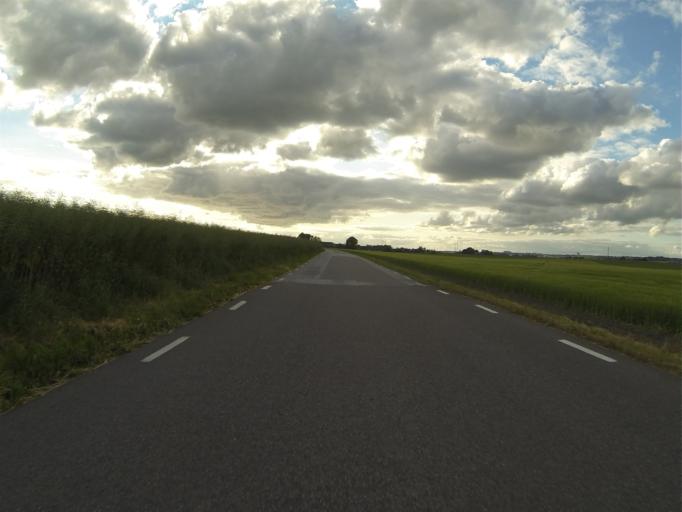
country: SE
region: Skane
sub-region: Staffanstorps Kommun
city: Staffanstorp
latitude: 55.6615
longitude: 13.2569
